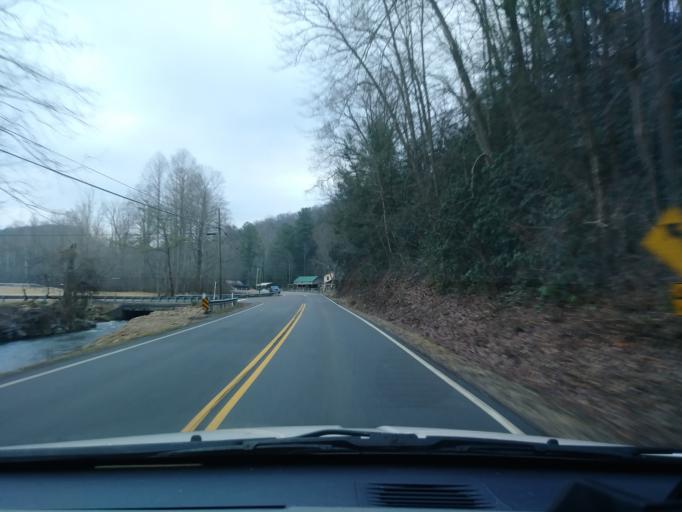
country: US
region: Tennessee
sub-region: Unicoi County
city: Unicoi
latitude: 36.1760
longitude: -82.2918
